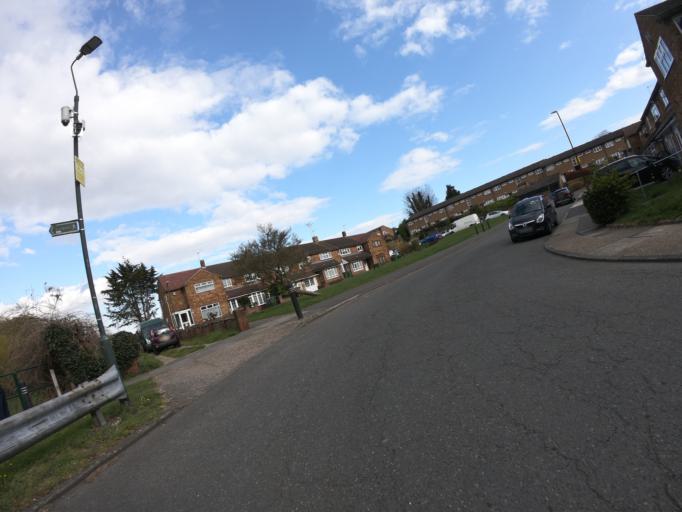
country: GB
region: England
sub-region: Greater London
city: Belvedere
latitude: 51.4801
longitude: 0.1487
